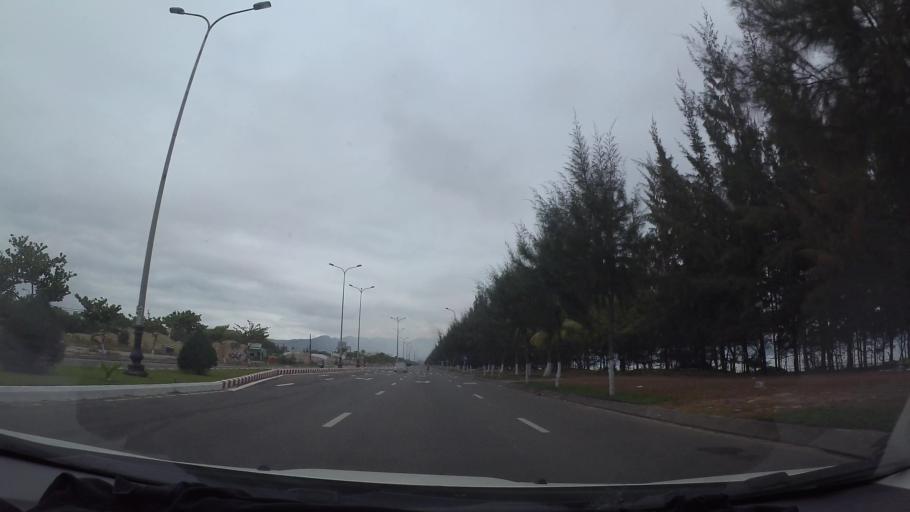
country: VN
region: Da Nang
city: Lien Chieu
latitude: 16.1016
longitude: 108.1397
